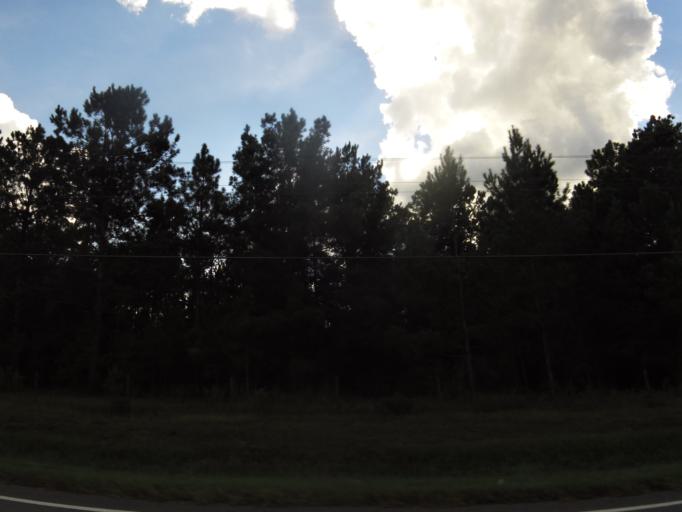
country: US
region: Georgia
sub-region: Lowndes County
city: Valdosta
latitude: 30.7782
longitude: -83.1538
